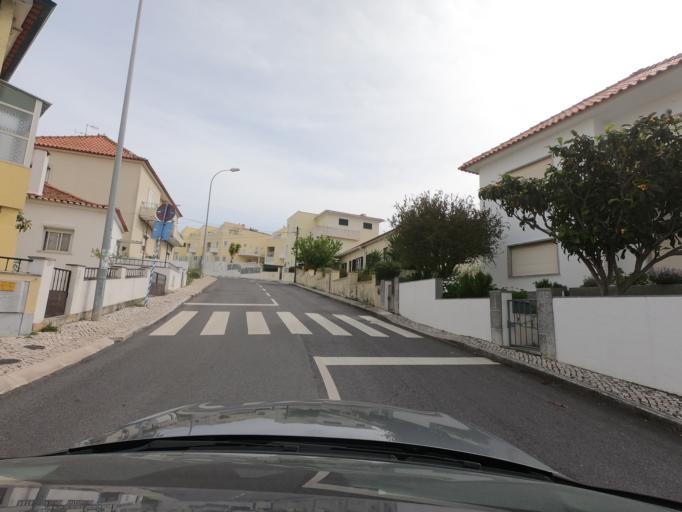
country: PT
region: Lisbon
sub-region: Oeiras
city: Porto Salvo
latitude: 38.7180
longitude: -9.2987
